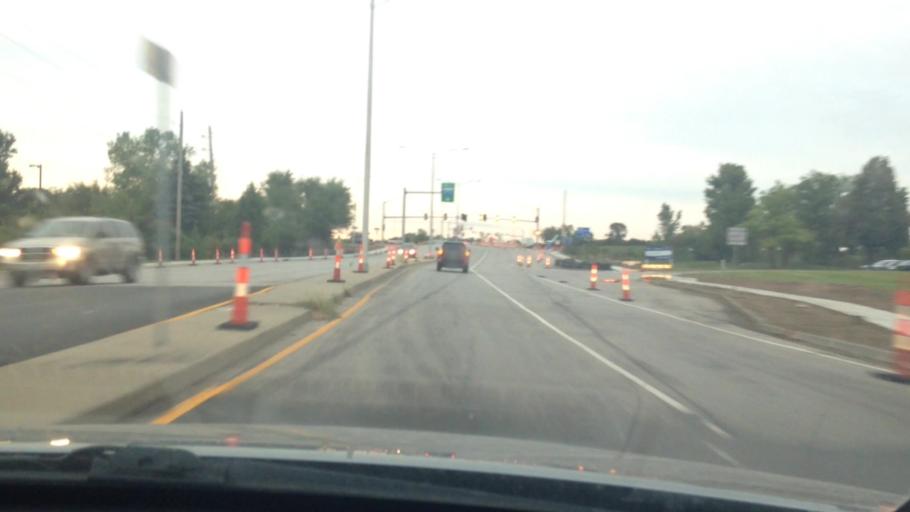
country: US
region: Missouri
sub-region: Jackson County
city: Lees Summit
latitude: 38.9419
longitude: -94.3782
